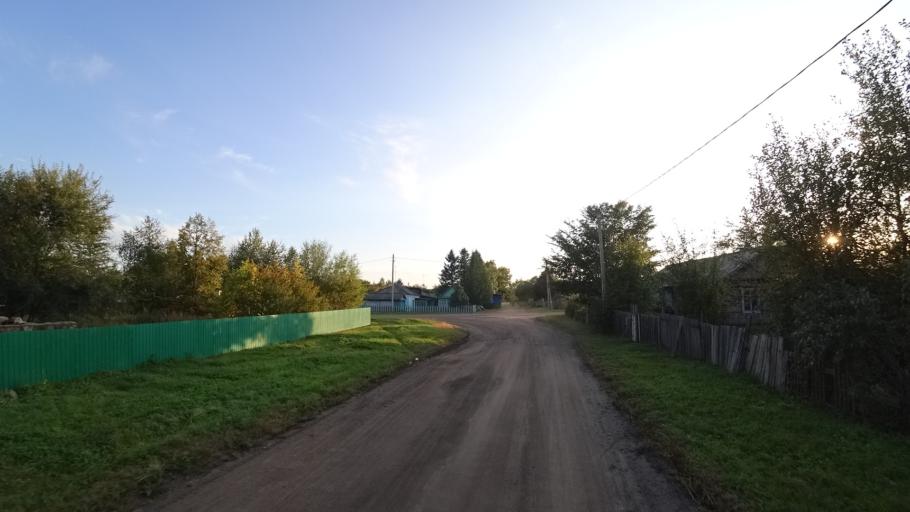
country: RU
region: Amur
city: Arkhara
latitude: 49.3612
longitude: 130.1150
